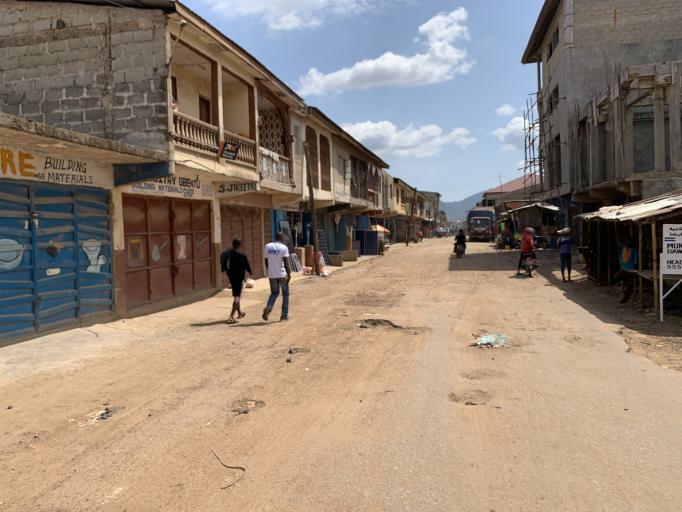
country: SL
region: Western Area
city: Waterloo
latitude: 8.3296
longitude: -13.0509
